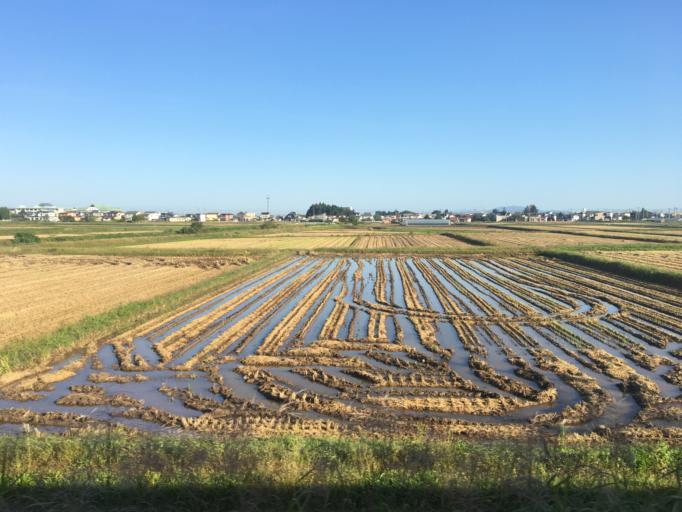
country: JP
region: Aomori
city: Kuroishi
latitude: 40.5807
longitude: 140.5571
